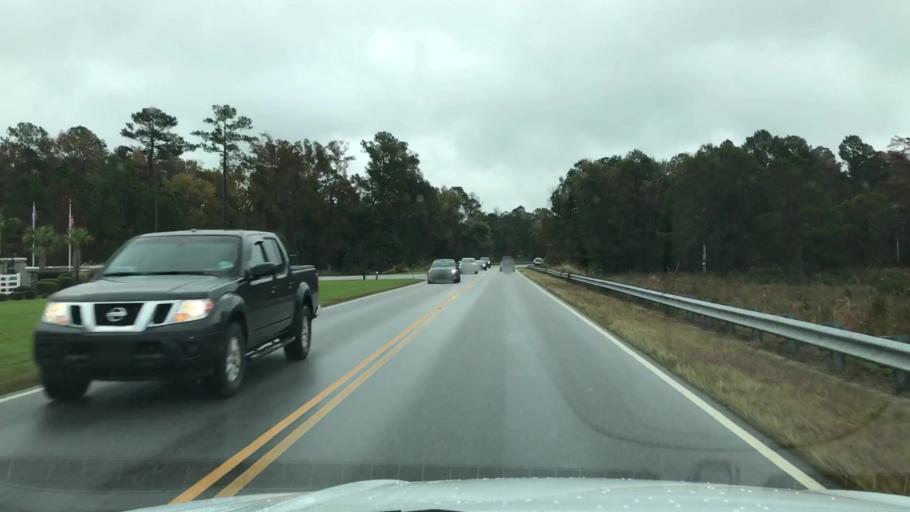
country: US
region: South Carolina
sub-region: Horry County
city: Myrtle Beach
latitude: 33.7547
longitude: -78.8760
